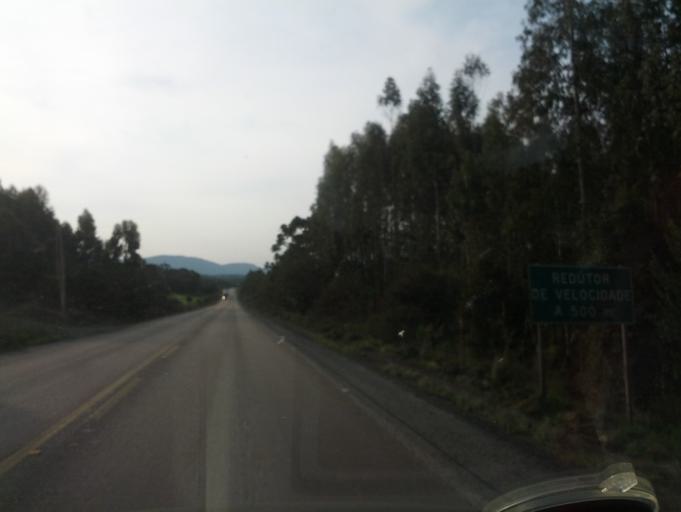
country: BR
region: Santa Catarina
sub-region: Otacilio Costa
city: Otacilio Costa
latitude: -27.4082
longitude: -50.1282
